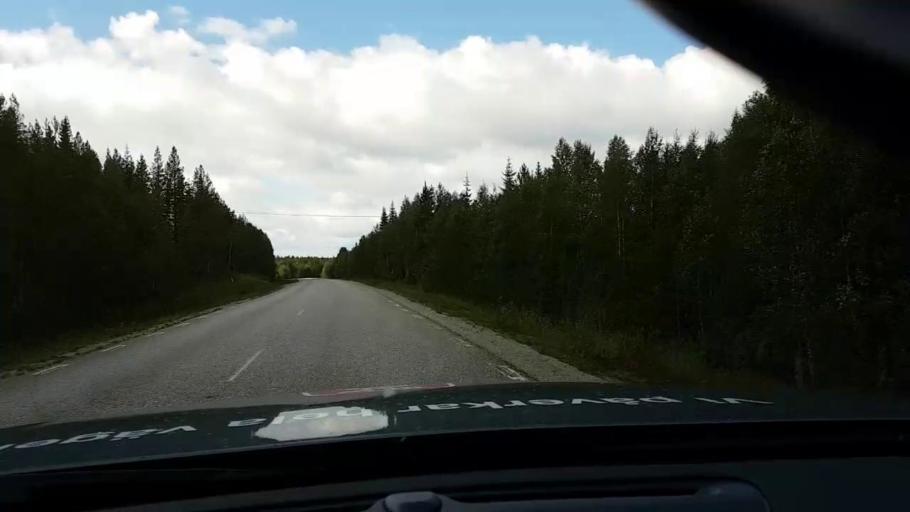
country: SE
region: Vaesterbotten
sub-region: Asele Kommun
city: Asele
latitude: 63.9292
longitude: 17.3056
